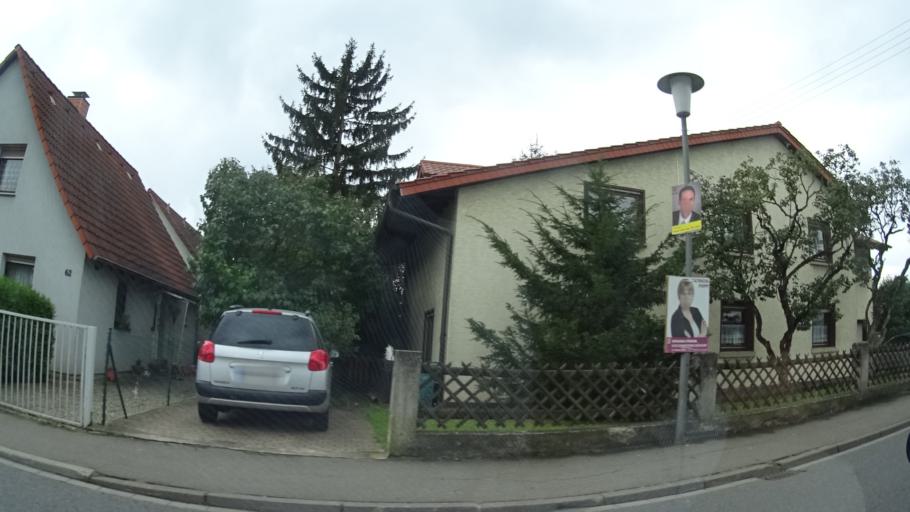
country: DE
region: Baden-Wuerttemberg
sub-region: Karlsruhe Region
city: Eppelheim
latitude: 49.3949
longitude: 8.6298
